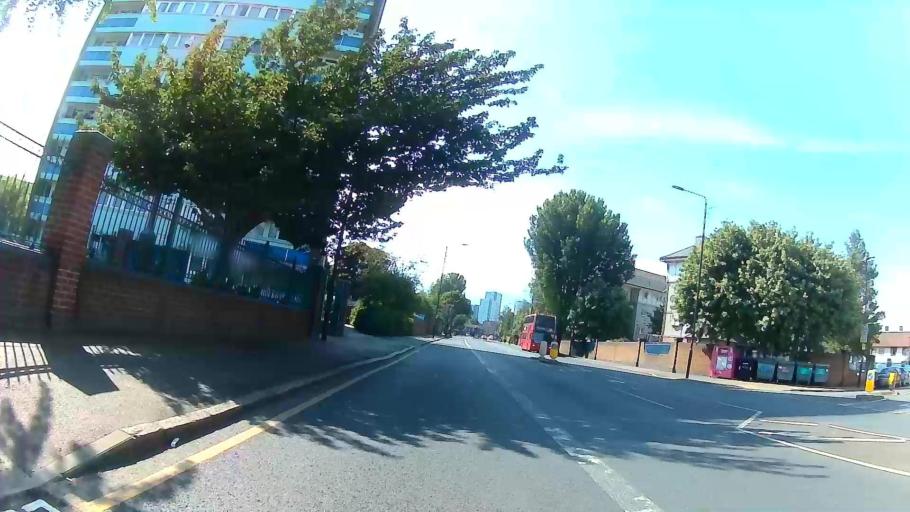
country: GB
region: England
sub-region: Greater London
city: Poplar
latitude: 51.5342
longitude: 0.0111
